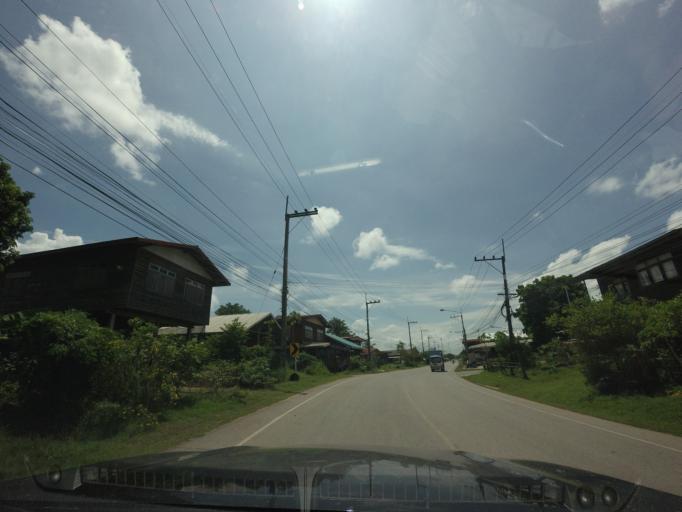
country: TH
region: Nong Khai
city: Pho Tak
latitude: 17.7791
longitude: 102.3947
